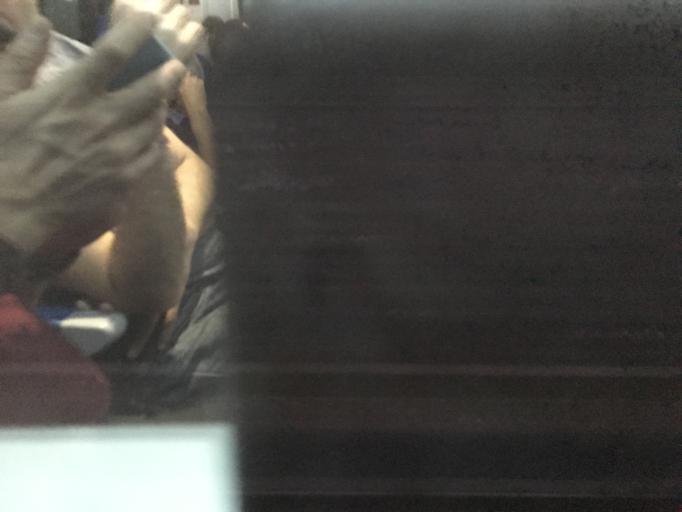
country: TR
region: Kocaeli
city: Derince
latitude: 40.7510
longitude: 29.8157
